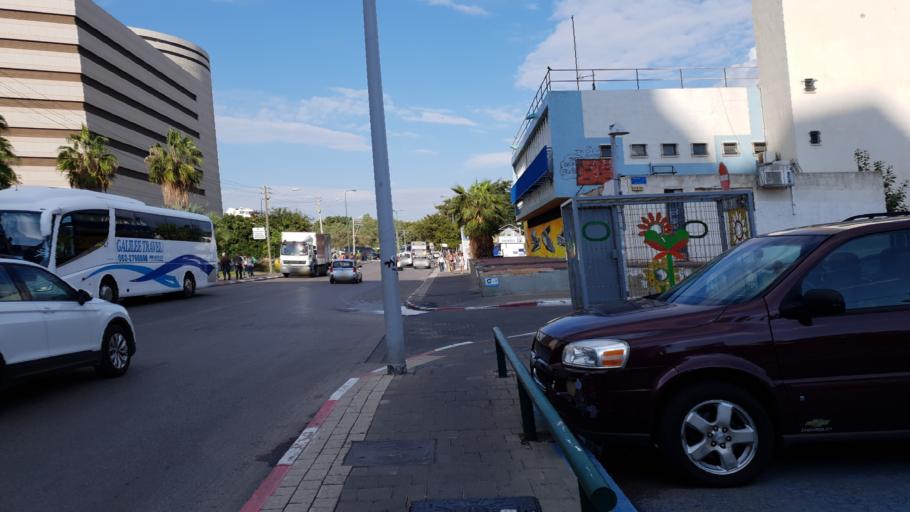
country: IL
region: Tel Aviv
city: Yafo
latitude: 32.0643
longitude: 34.7640
